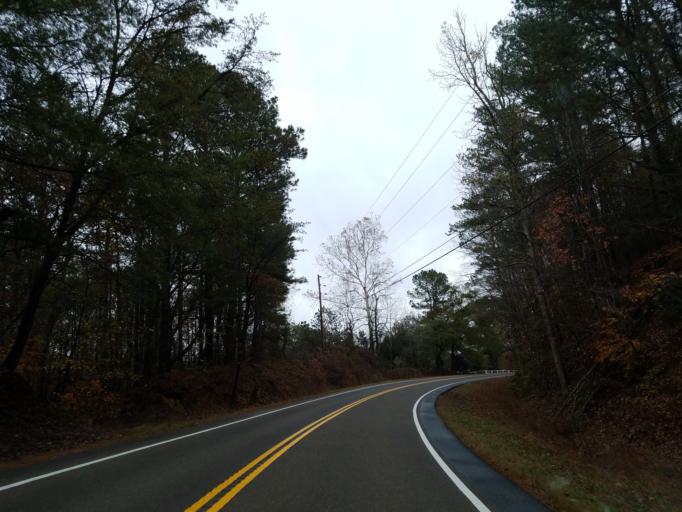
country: US
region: Georgia
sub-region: Cherokee County
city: Canton
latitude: 34.2641
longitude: -84.5945
